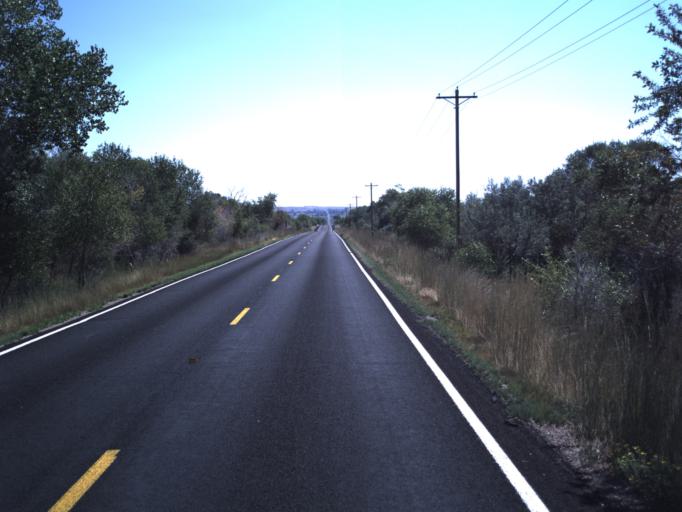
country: US
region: Utah
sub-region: Duchesne County
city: Roosevelt
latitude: 40.4037
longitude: -109.8840
